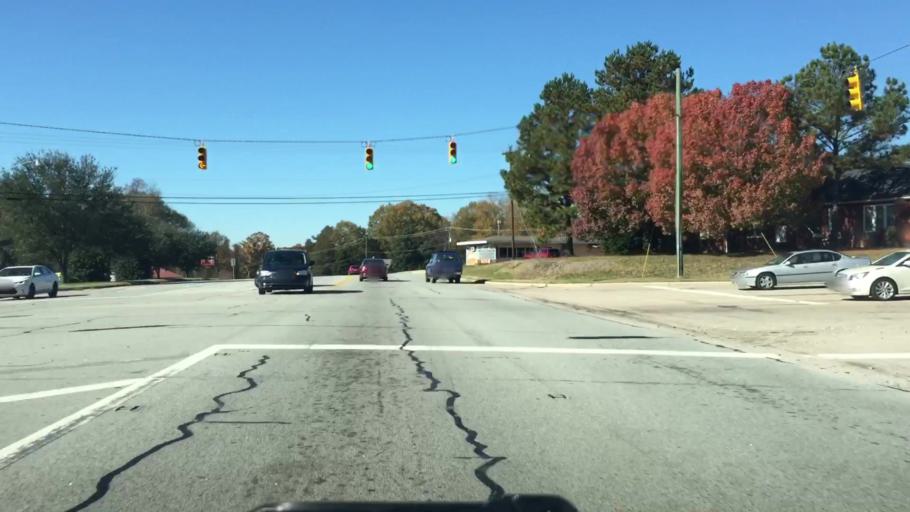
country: US
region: North Carolina
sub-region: Rowan County
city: Salisbury
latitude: 35.6632
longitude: -80.5039
